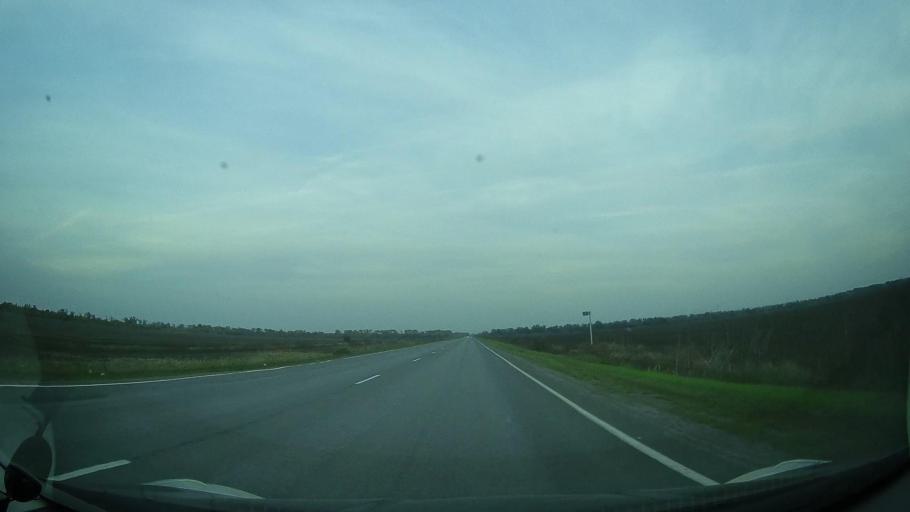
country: RU
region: Rostov
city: Ol'ginskaya
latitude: 47.1301
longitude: 39.9151
